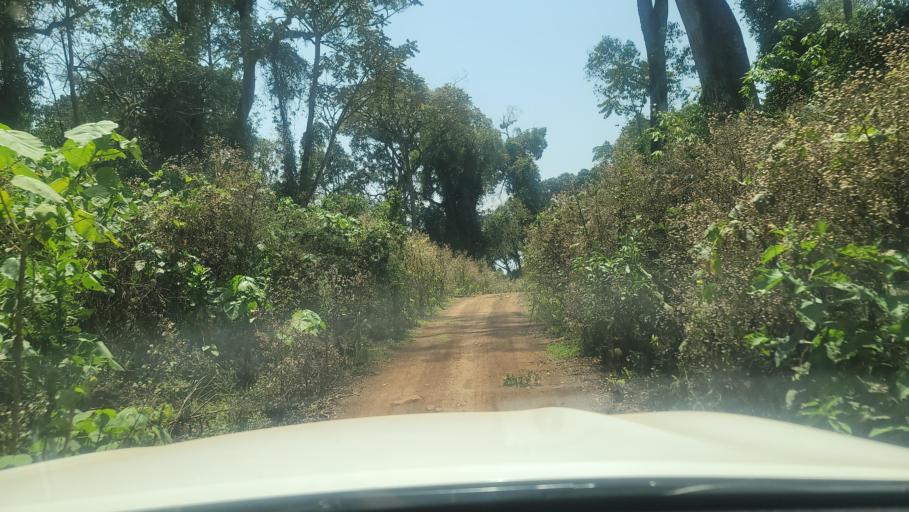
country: ET
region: Southern Nations, Nationalities, and People's Region
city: Bonga
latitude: 7.5488
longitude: 36.1751
